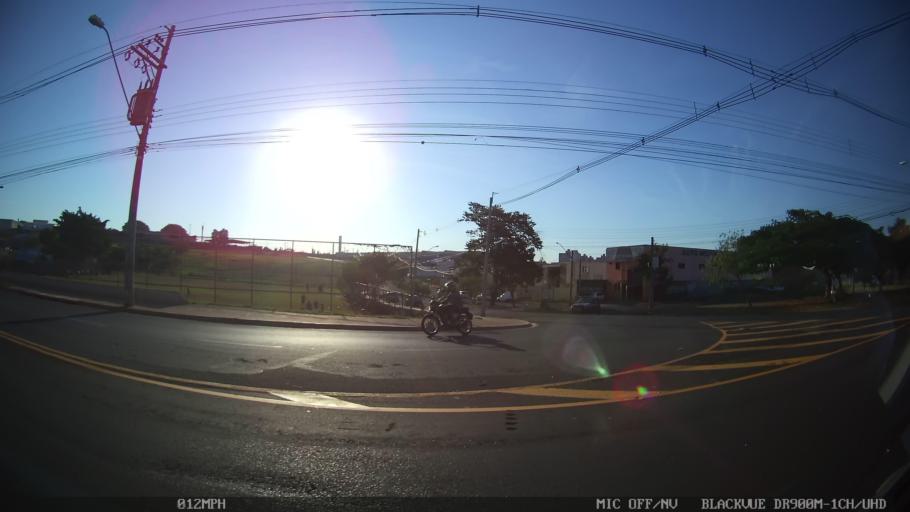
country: BR
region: Sao Paulo
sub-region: Sao Jose Do Rio Preto
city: Sao Jose do Rio Preto
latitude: -20.7909
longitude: -49.3487
